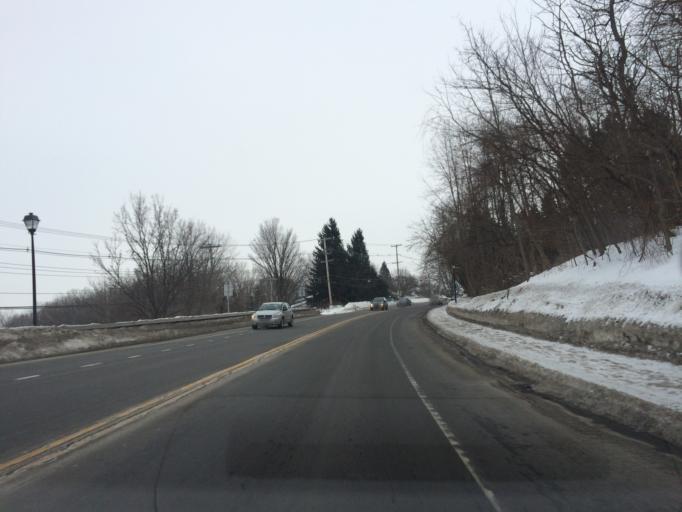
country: US
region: New York
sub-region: Monroe County
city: Fairport
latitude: 43.0961
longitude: -77.4326
